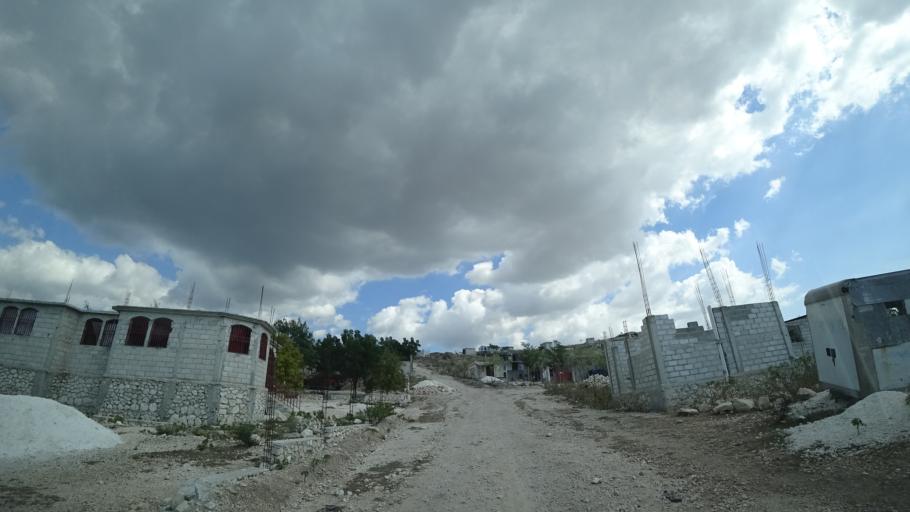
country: HT
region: Ouest
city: Cabaret
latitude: 18.6781
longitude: -72.3156
